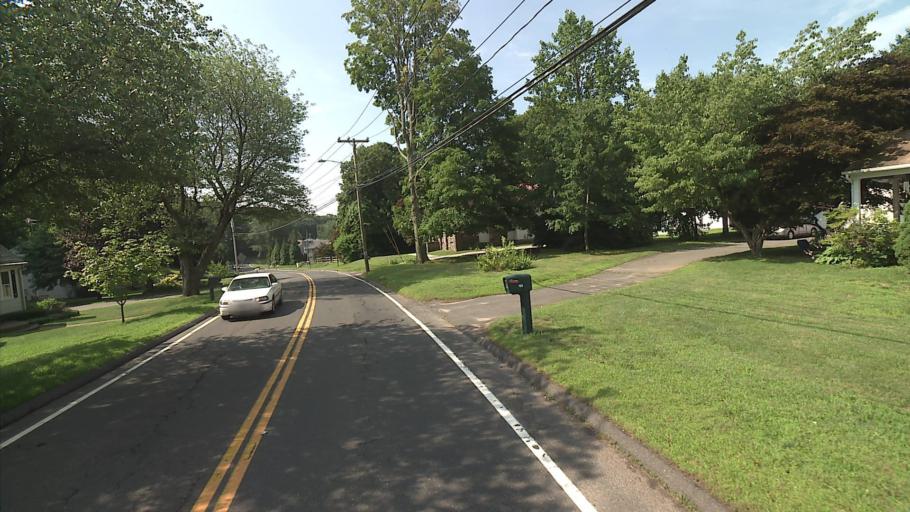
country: US
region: Connecticut
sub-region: New Haven County
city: Wolcott
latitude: 41.5634
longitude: -72.9475
